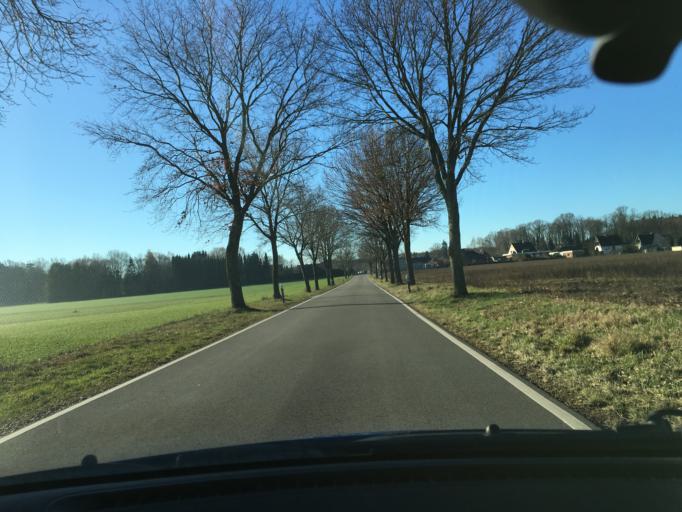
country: DE
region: Lower Saxony
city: Barnstedt
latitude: 53.1457
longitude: 10.3738
